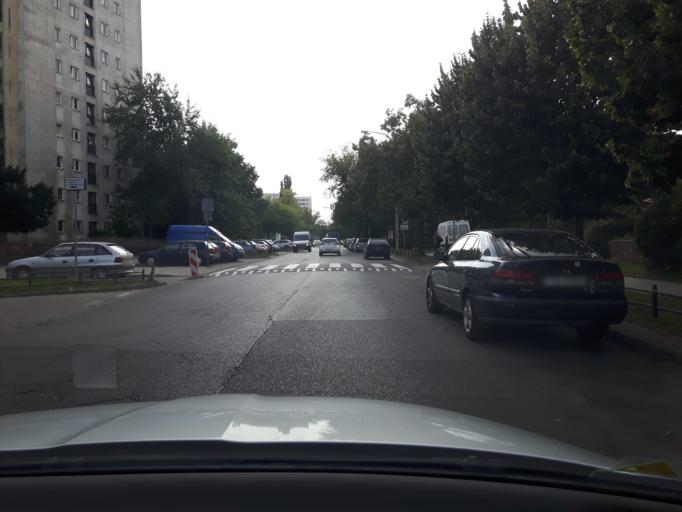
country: PL
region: Masovian Voivodeship
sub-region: Warszawa
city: Mokotow
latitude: 52.1897
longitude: 21.0537
